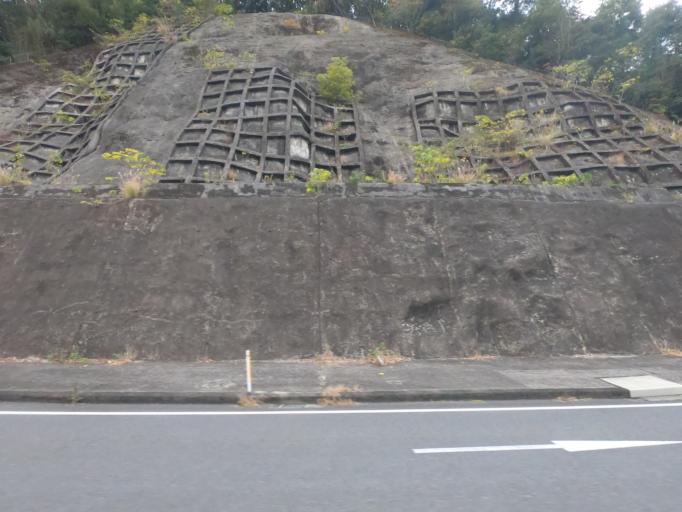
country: JP
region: Kumamoto
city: Minamata
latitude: 32.2570
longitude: 130.5095
